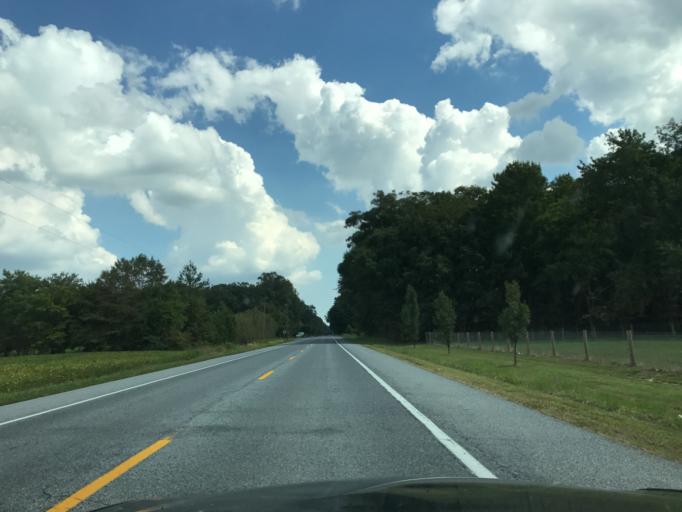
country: US
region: Delaware
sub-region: Kent County
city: Clayton
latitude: 39.1951
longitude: -75.8071
